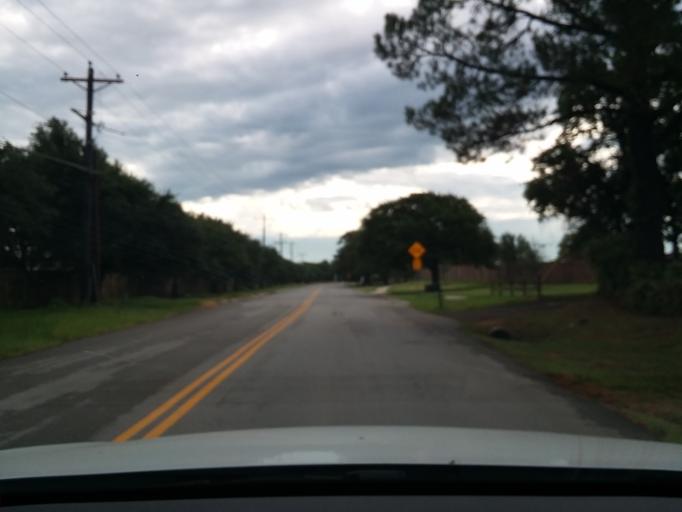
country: US
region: Texas
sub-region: Denton County
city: Double Oak
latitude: 33.0626
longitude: -97.0838
